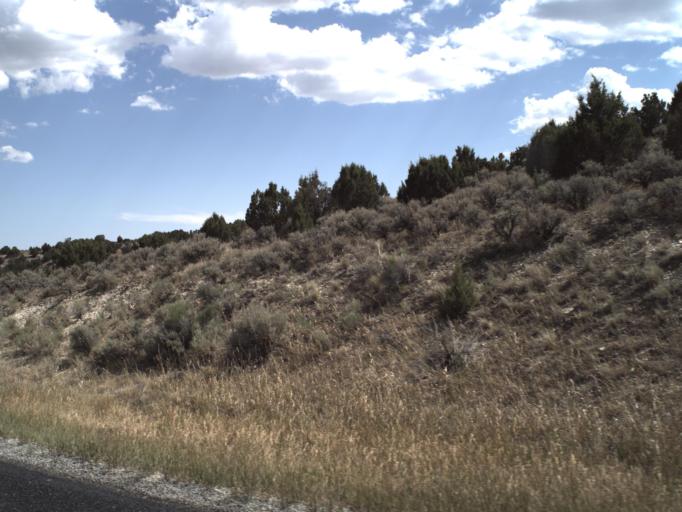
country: US
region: Idaho
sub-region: Minidoka County
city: Rupert
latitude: 41.9827
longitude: -113.1710
